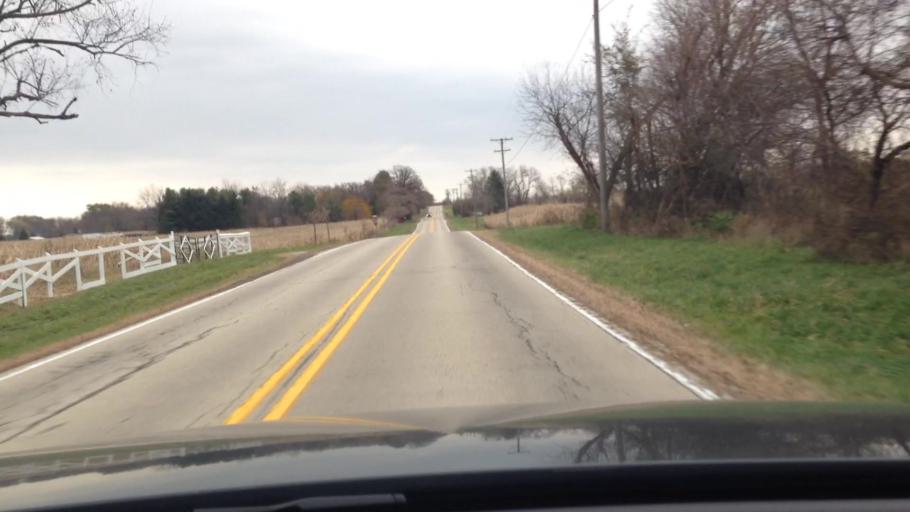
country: US
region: Illinois
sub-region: McHenry County
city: Woodstock
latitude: 42.2766
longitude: -88.4630
